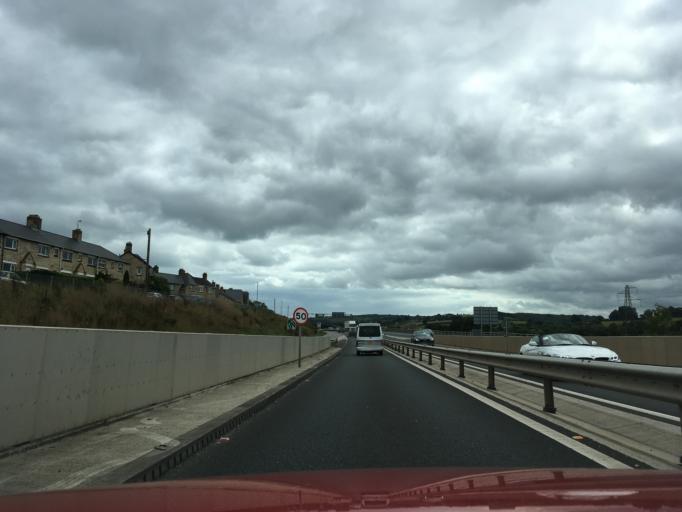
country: GB
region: England
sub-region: Devon
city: Newton Abbot
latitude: 50.5228
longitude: -3.5930
